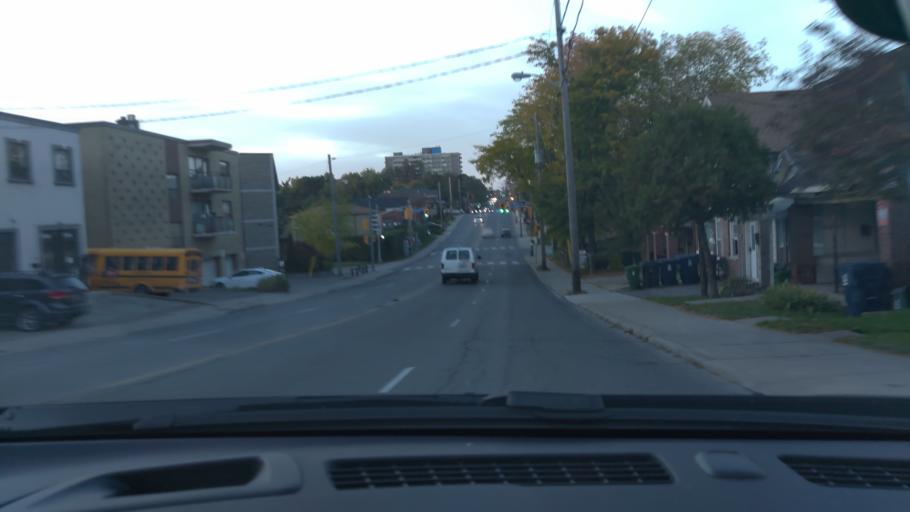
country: CA
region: Ontario
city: Toronto
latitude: 43.6879
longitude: -79.4470
